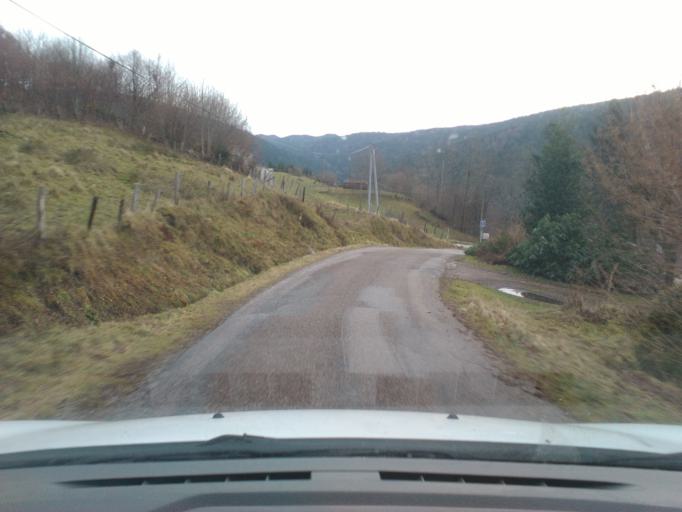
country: FR
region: Lorraine
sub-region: Departement des Vosges
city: La Bresse
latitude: 47.9742
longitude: 6.8575
